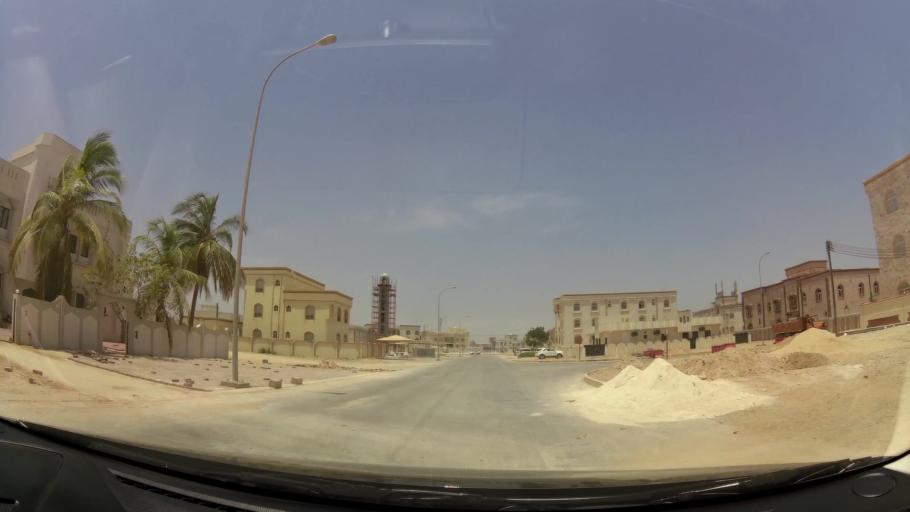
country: OM
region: Zufar
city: Salalah
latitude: 17.0732
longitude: 54.1590
